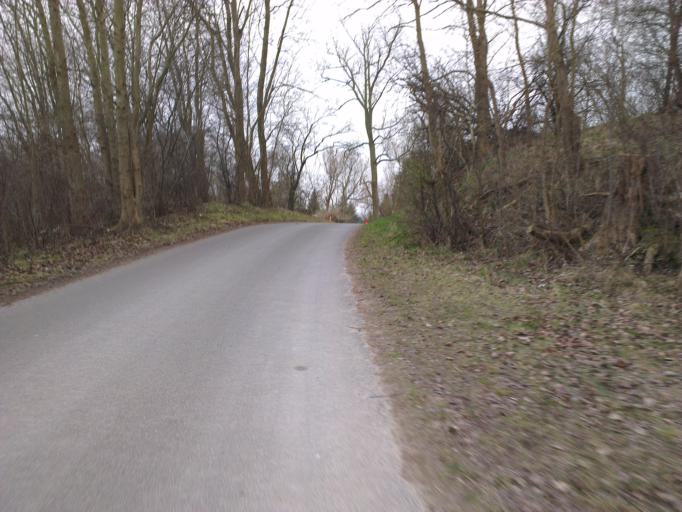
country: DK
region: Capital Region
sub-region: Frederikssund Kommune
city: Frederikssund
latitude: 55.7925
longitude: 12.0546
